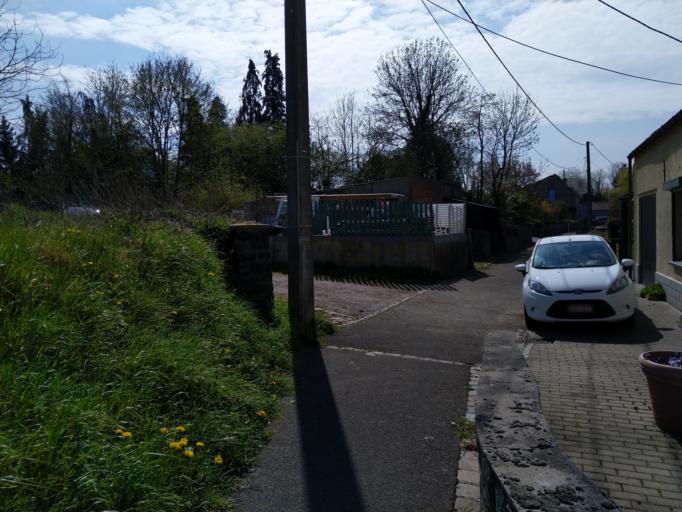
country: BE
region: Wallonia
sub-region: Province du Hainaut
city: Mons
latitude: 50.4781
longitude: 4.0119
